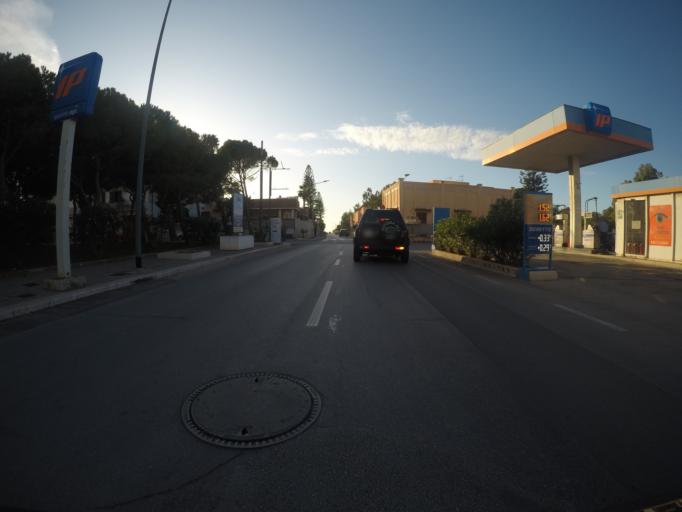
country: IT
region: Sicily
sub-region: Palermo
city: Isola delle Femmine
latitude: 38.1988
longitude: 13.2468
